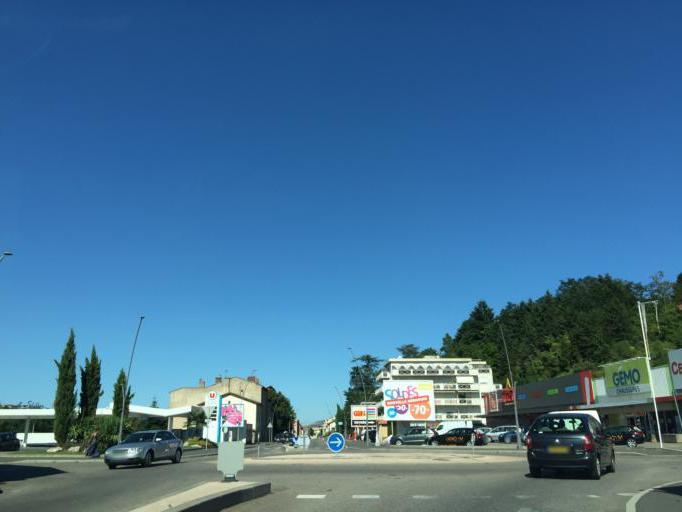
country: FR
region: Rhone-Alpes
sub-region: Departement de la Loire
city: Saint-Chamond
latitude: 45.4831
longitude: 4.5333
